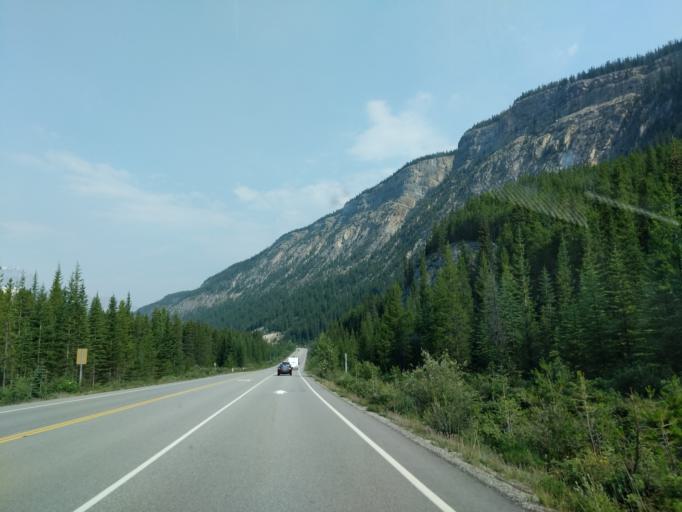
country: CA
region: Alberta
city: Lake Louise
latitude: 51.8429
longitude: -116.6190
